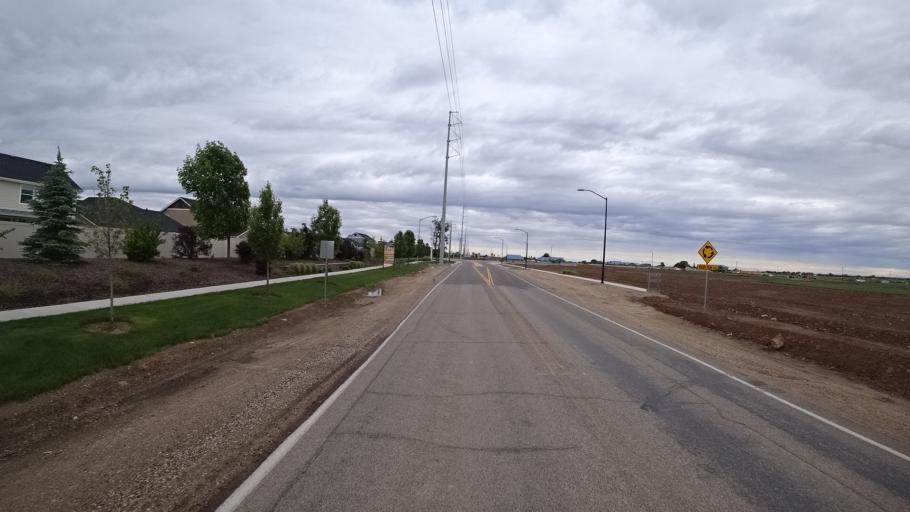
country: US
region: Idaho
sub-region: Ada County
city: Star
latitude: 43.6485
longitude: -116.4618
